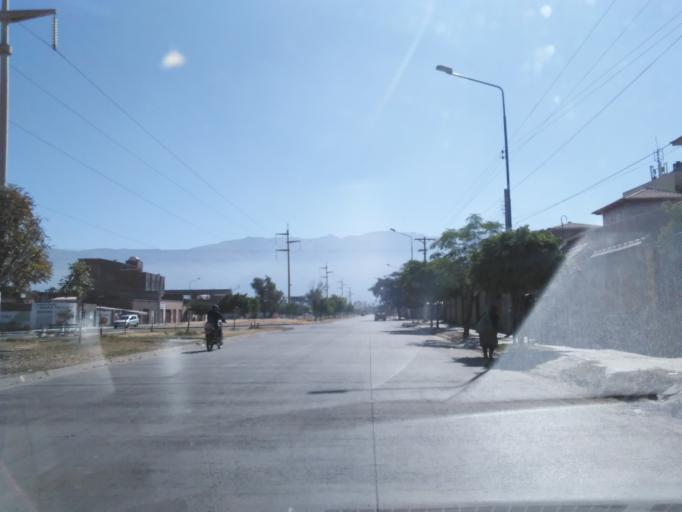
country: BO
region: Cochabamba
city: Cochabamba
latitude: -17.3999
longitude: -66.1862
